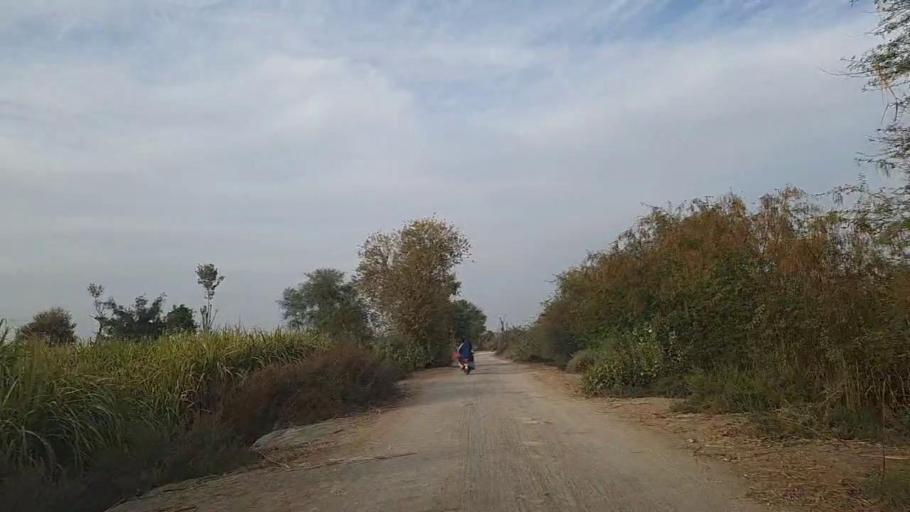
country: PK
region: Sindh
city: Daur
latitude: 26.5239
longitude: 68.4073
